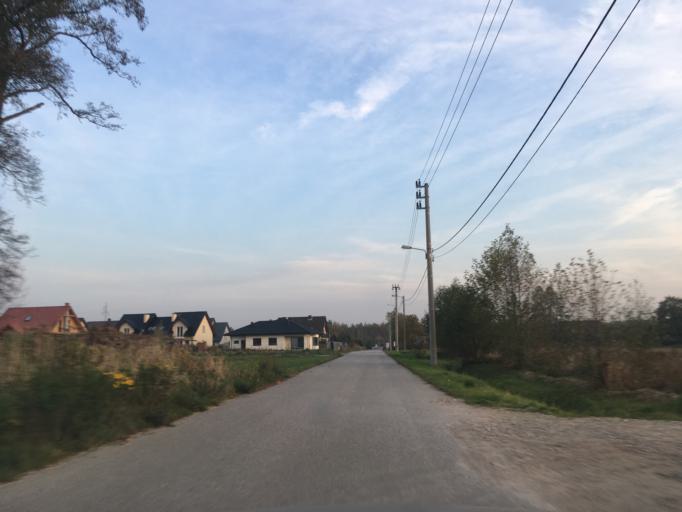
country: PL
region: Masovian Voivodeship
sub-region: Powiat piaseczynski
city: Lesznowola
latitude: 52.0492
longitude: 20.9278
